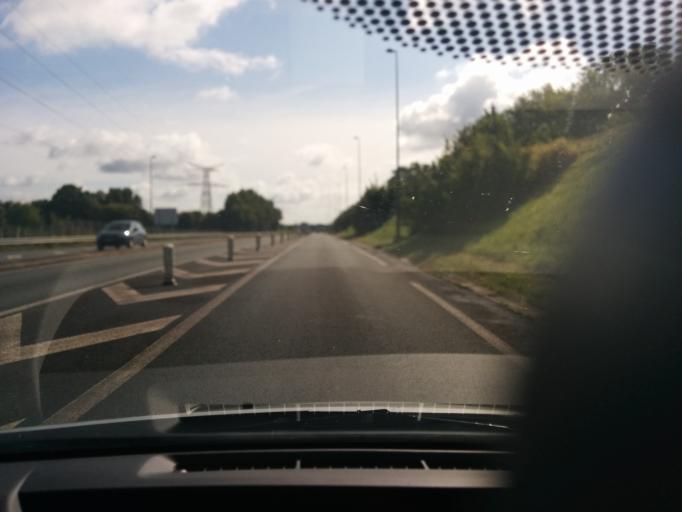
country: FR
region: Pays de la Loire
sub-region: Departement de Maine-et-Loire
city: Trelaze
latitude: 47.4730
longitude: -0.4907
